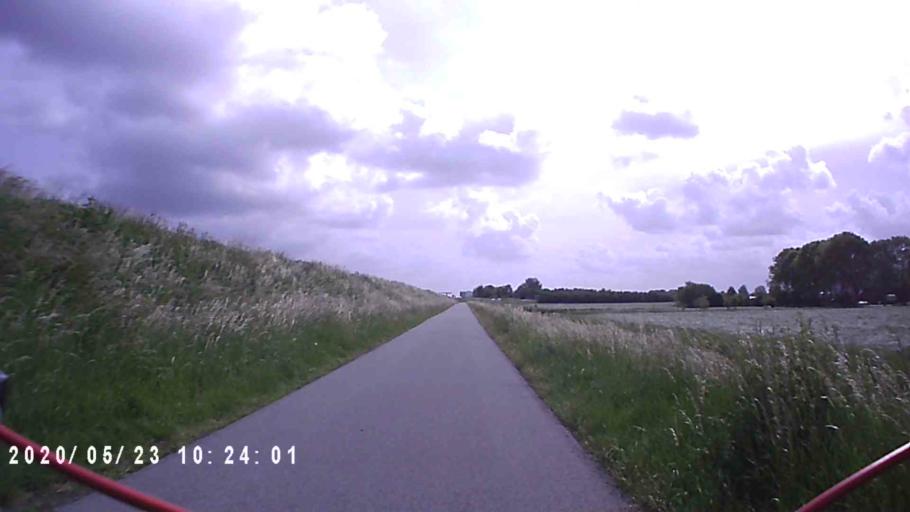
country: NL
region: Groningen
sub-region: Gemeente Appingedam
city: Appingedam
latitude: 53.3037
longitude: 6.8405
